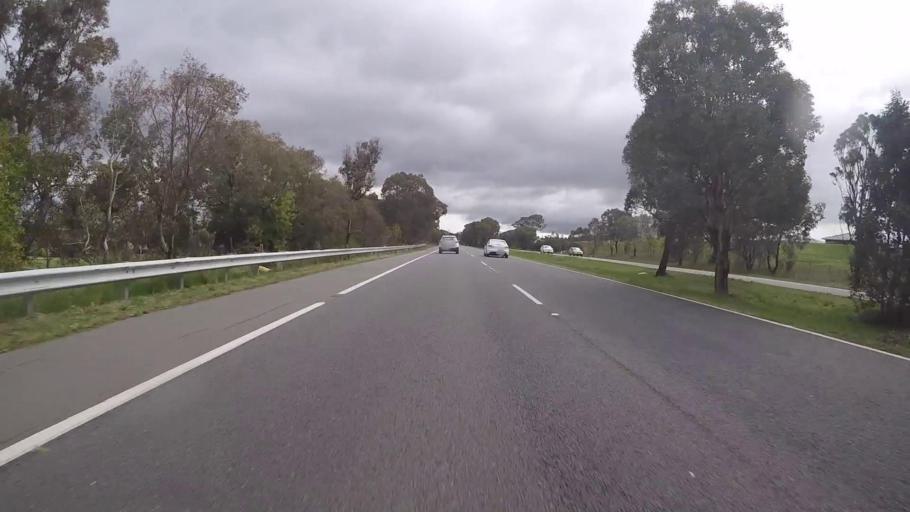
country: AU
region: Australian Capital Territory
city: Kaleen
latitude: -35.2086
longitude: 149.1063
